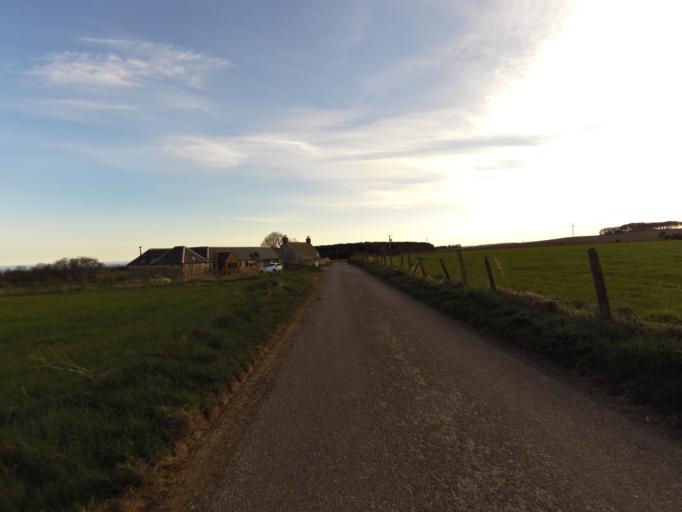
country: GB
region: Scotland
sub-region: Aberdeenshire
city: Stonehaven
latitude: 56.9321
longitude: -2.2259
